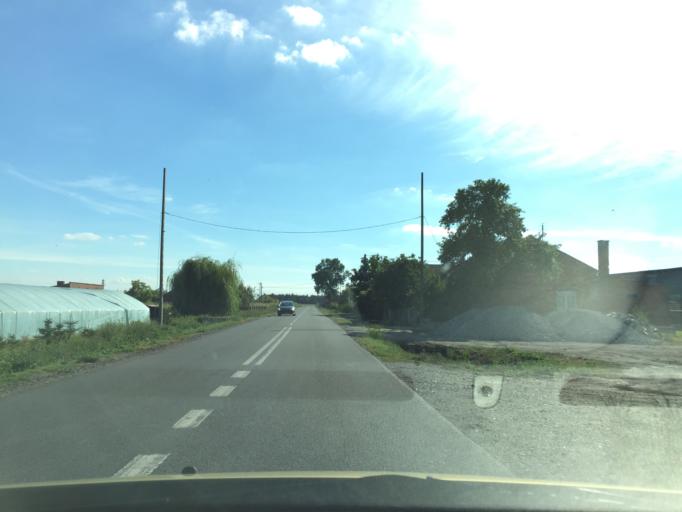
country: PL
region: Greater Poland Voivodeship
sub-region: Powiat kaliski
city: Stawiszyn
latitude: 51.9336
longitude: 18.1477
